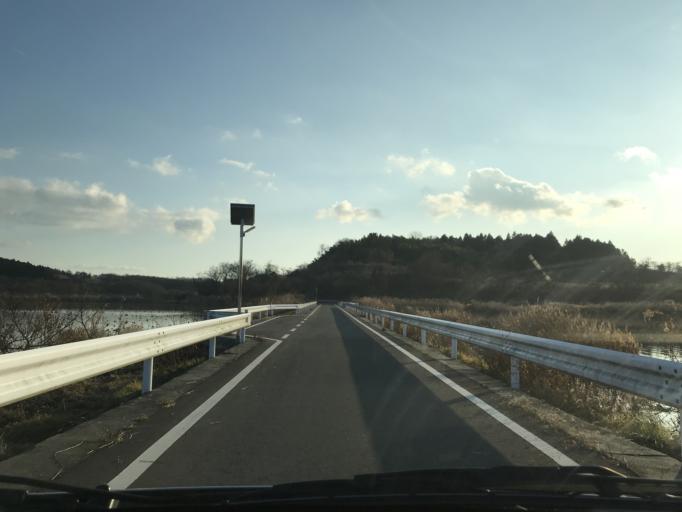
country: JP
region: Miyagi
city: Wakuya
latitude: 38.6893
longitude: 141.1066
